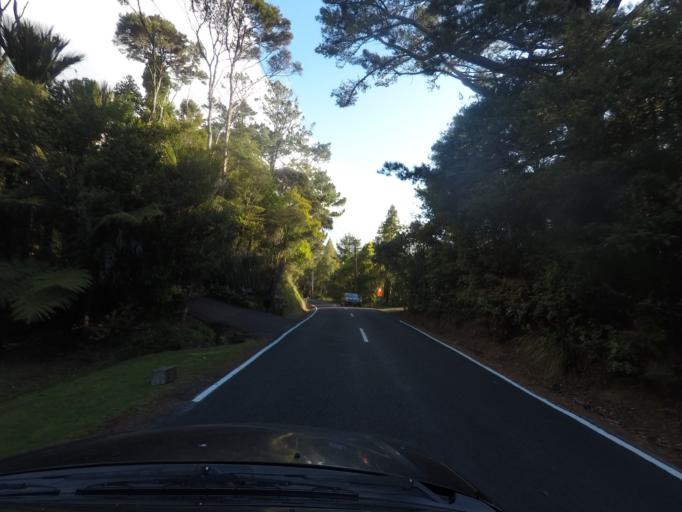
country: NZ
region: Auckland
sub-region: Auckland
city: Titirangi
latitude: -36.9357
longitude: 174.6185
